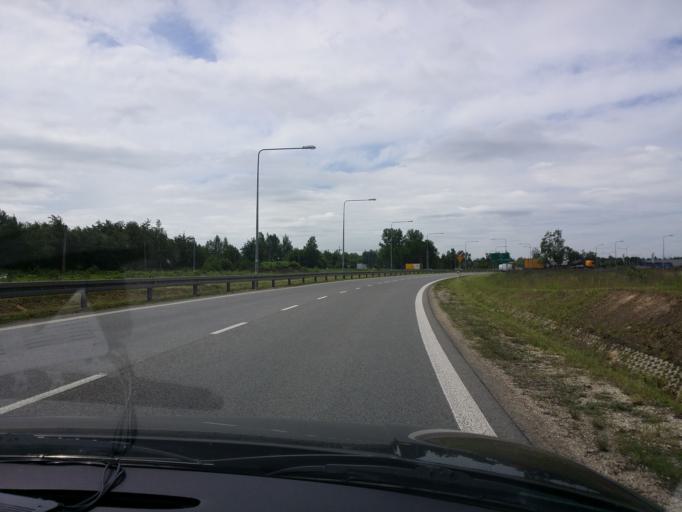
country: PL
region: Masovian Voivodeship
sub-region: Powiat radomski
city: Trablice
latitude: 51.3601
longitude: 21.1334
